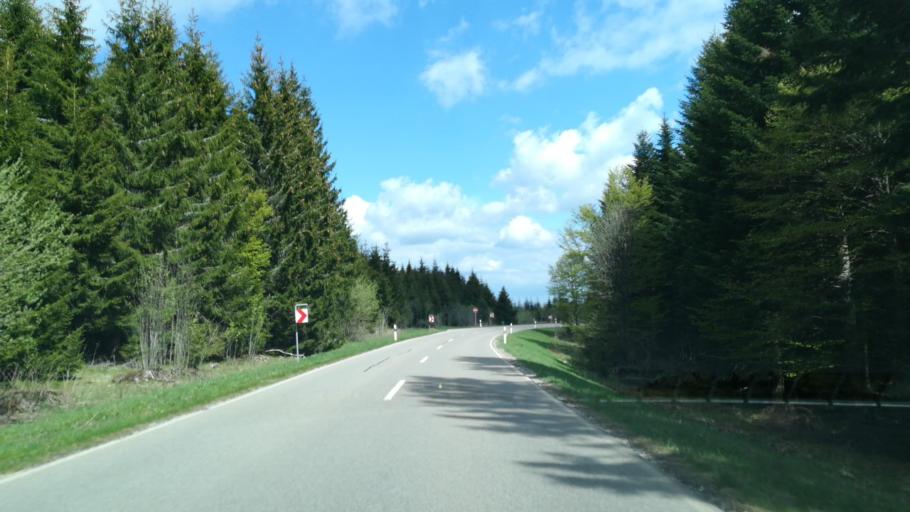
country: DE
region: Baden-Wuerttemberg
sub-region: Freiburg Region
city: Lenzkirch
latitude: 47.8332
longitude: 8.2302
